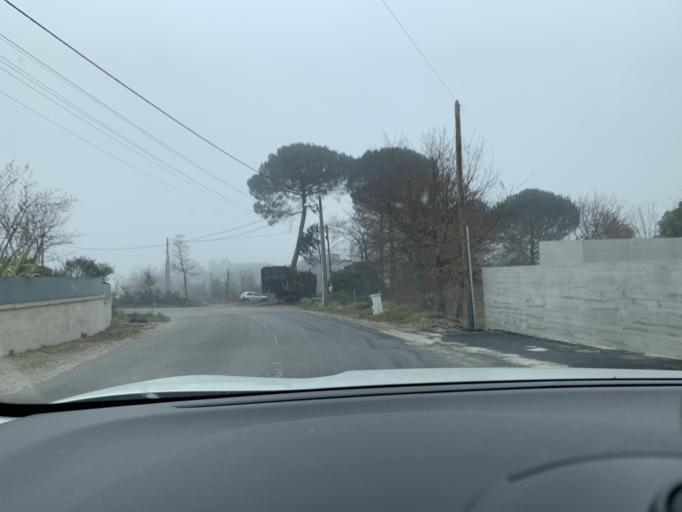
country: PT
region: Viseu
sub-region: Viseu
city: Viseu
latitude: 40.6286
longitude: -7.9202
